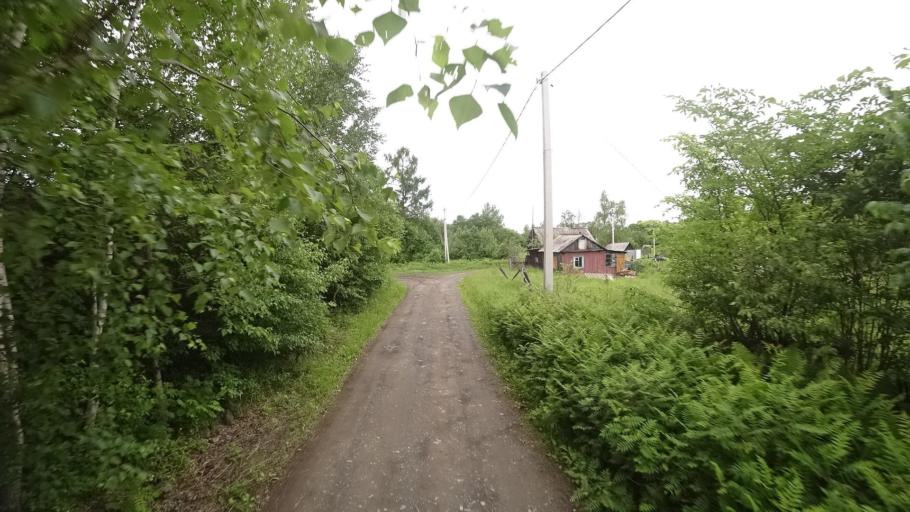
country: RU
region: Khabarovsk Krai
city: Amursk
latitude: 49.9036
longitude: 136.1359
